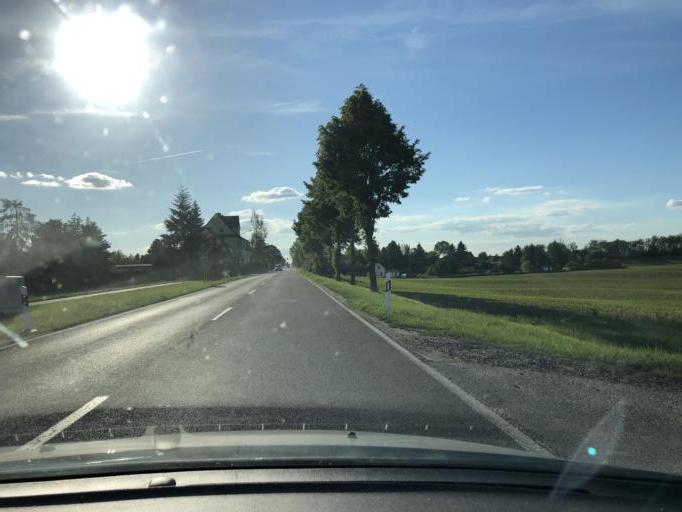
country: DE
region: Thuringia
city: Kriebitzsch
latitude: 51.0292
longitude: 12.3411
